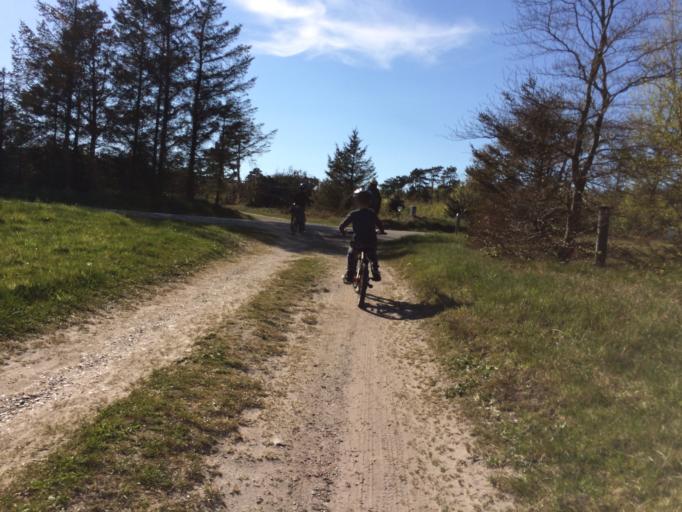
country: DK
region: Central Jutland
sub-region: Struer Kommune
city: Struer
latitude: 56.5424
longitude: 8.6261
